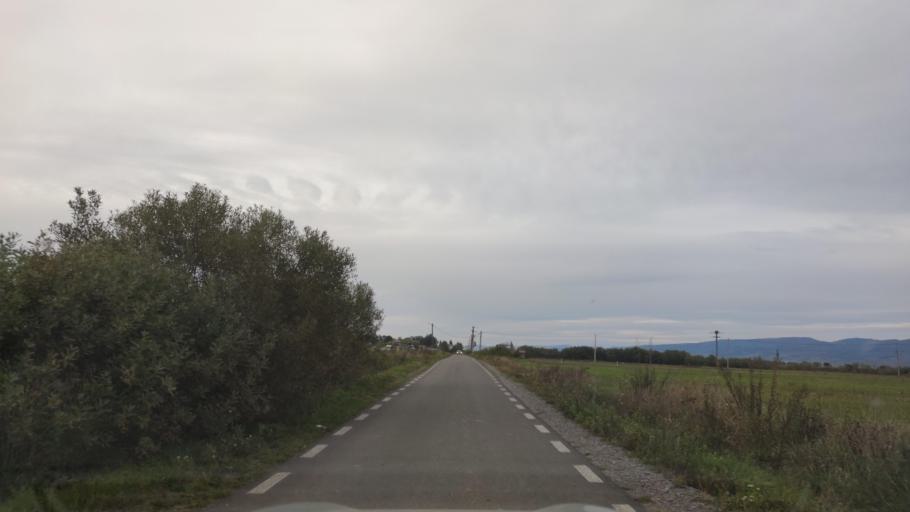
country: RO
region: Harghita
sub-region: Comuna Remetea
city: Remetea
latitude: 46.8086
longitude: 25.4231
